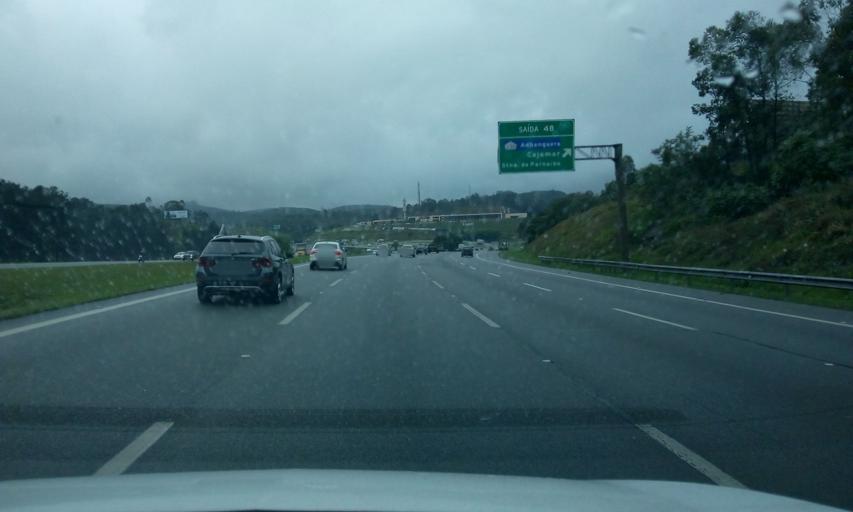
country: BR
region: Sao Paulo
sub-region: Varzea Paulista
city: Varzea Paulista
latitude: -23.2555
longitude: -46.8700
